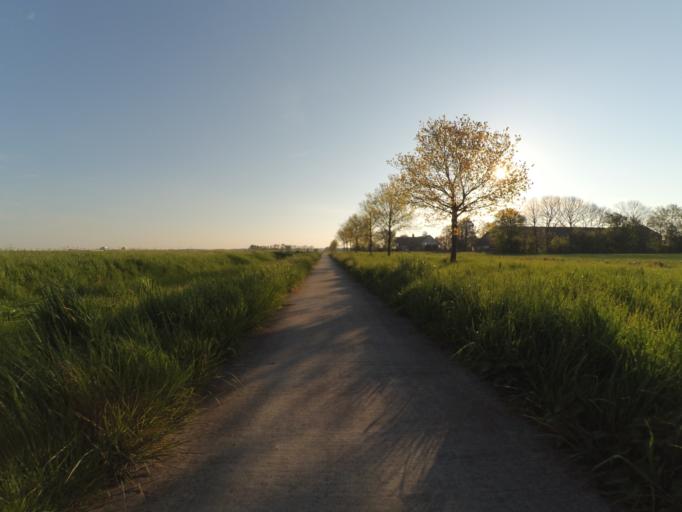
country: NL
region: Flevoland
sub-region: Gemeente Lelystad
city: Lelystad
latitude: 52.4593
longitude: 5.4870
